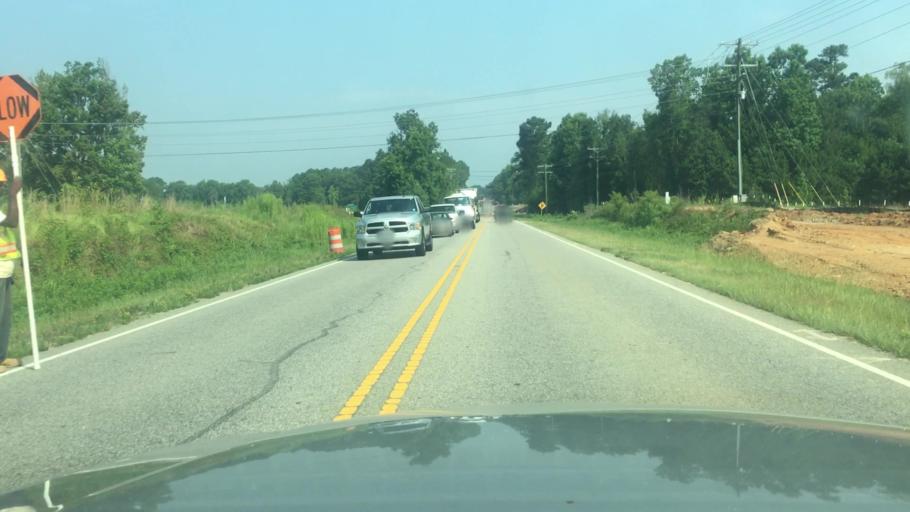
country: US
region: North Carolina
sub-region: Cumberland County
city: Hope Mills
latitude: 34.9280
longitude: -78.9123
